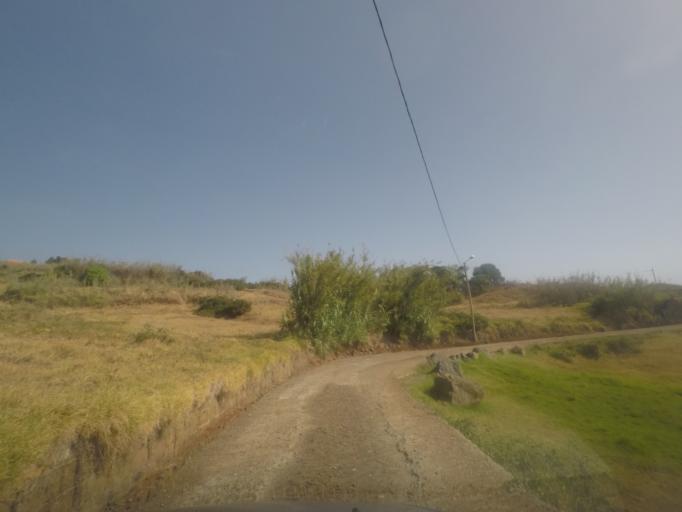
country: PT
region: Madeira
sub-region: Calheta
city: Faja da Ovelha
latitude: 32.8087
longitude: -17.2489
